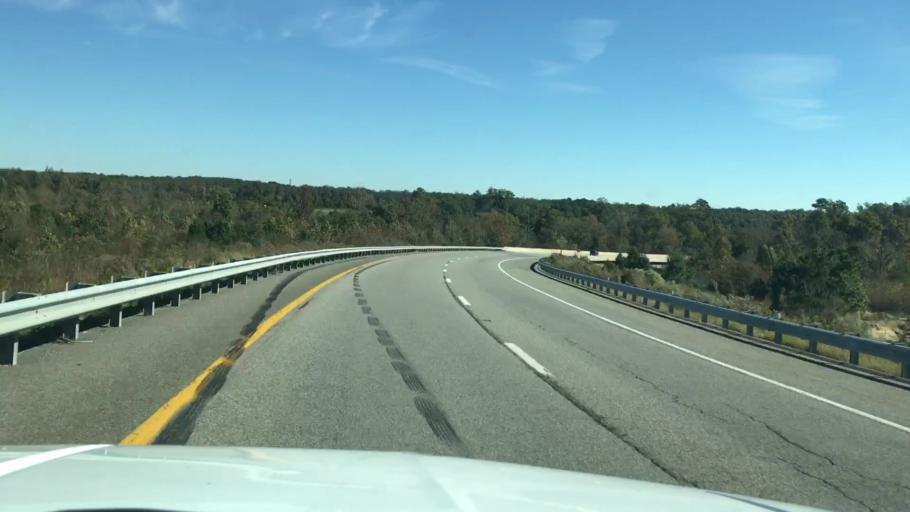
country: US
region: Virginia
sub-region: Henrico County
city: Short Pump
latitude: 37.6694
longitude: -77.6517
